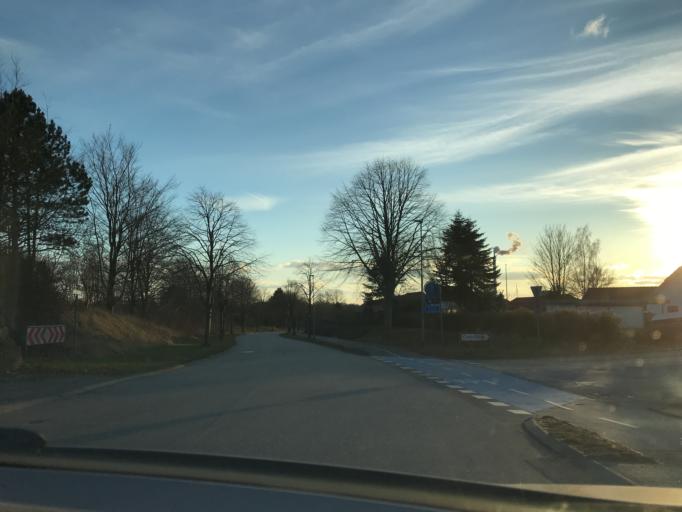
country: DK
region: South Denmark
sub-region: Middelfart Kommune
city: Norre Aby
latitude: 55.4590
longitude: 9.8847
